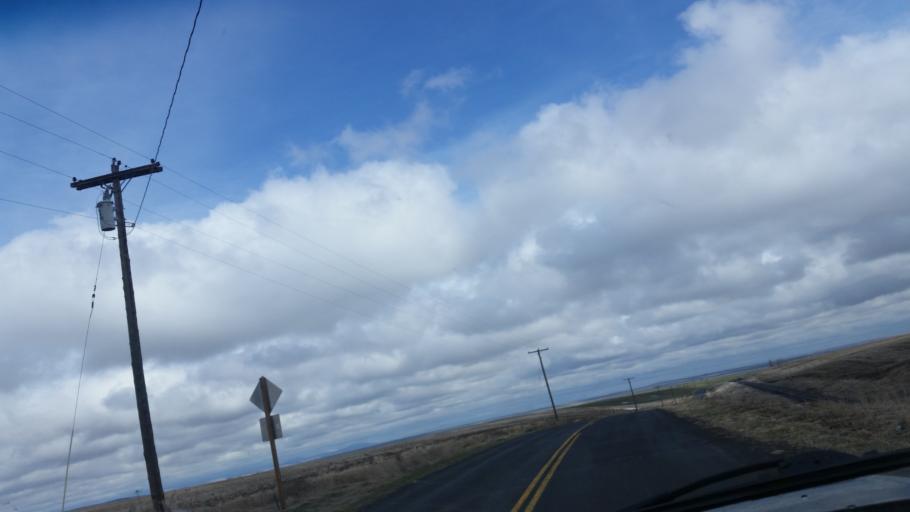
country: US
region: Washington
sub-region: Okanogan County
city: Coulee Dam
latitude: 47.7290
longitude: -119.0057
